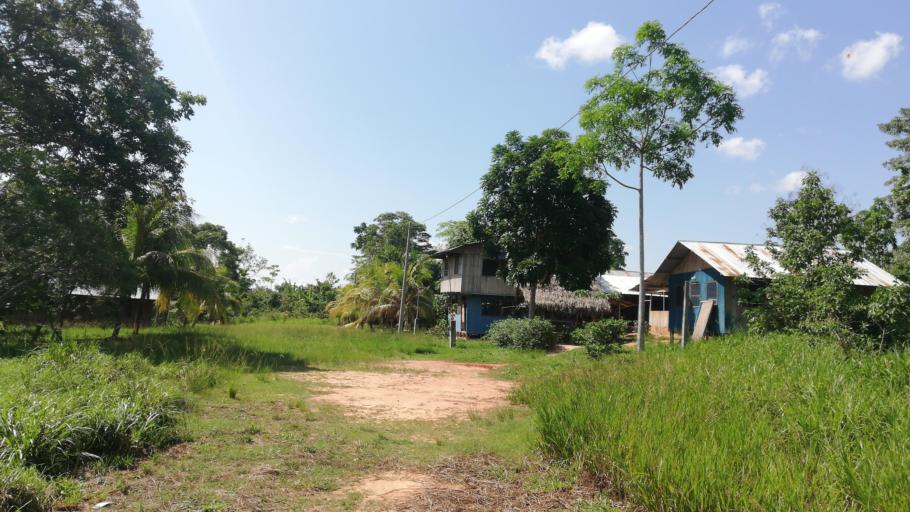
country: PE
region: Ucayali
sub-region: Provincia de Coronel Portillo
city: Puerto Callao
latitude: -8.2690
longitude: -74.6497
